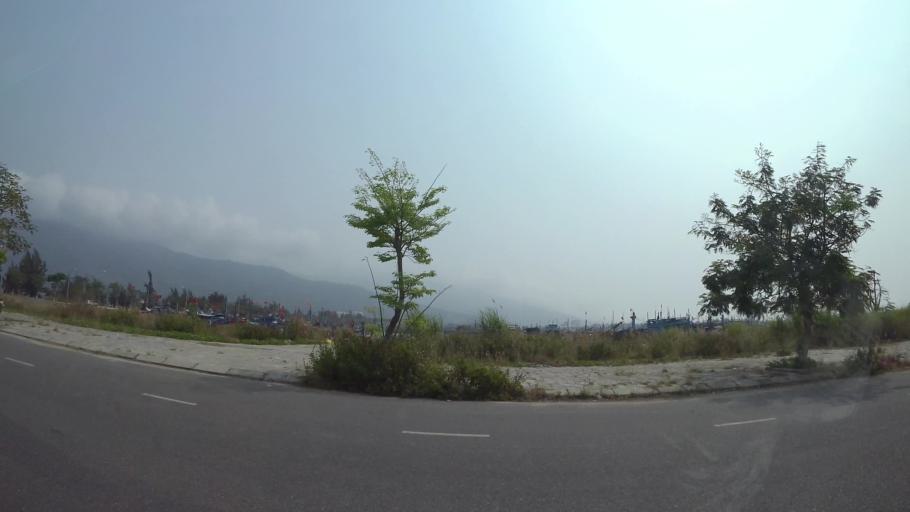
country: VN
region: Da Nang
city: Da Nang
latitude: 16.1011
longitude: 108.2347
